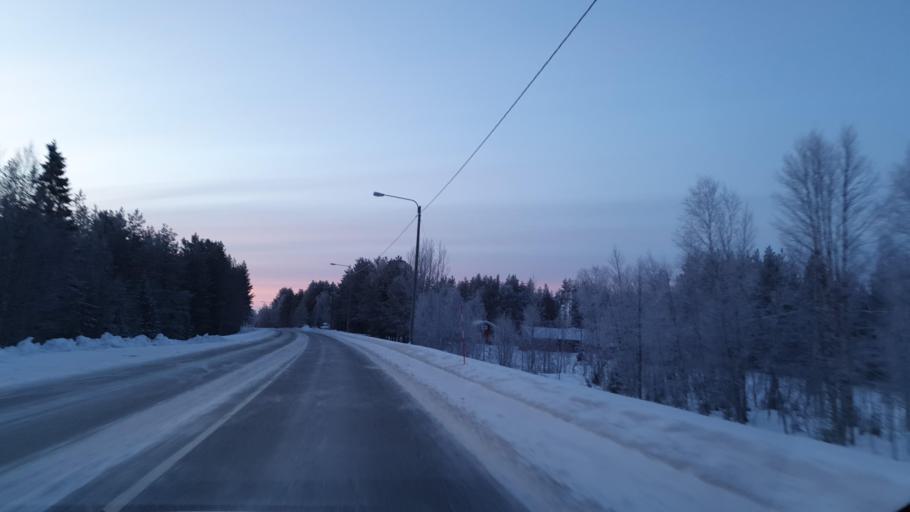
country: FI
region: Lapland
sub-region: Tunturi-Lappi
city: Kolari
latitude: 67.1080
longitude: 23.9868
